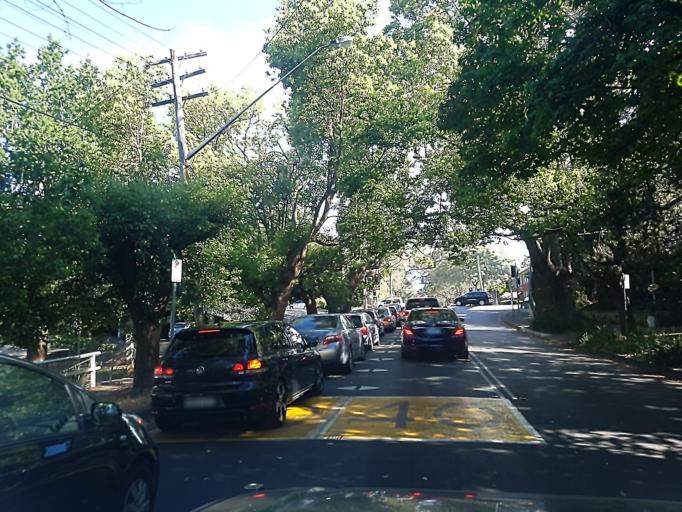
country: AU
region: New South Wales
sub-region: Ku-ring-gai
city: North Wahroonga
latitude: -33.7190
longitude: 151.1160
